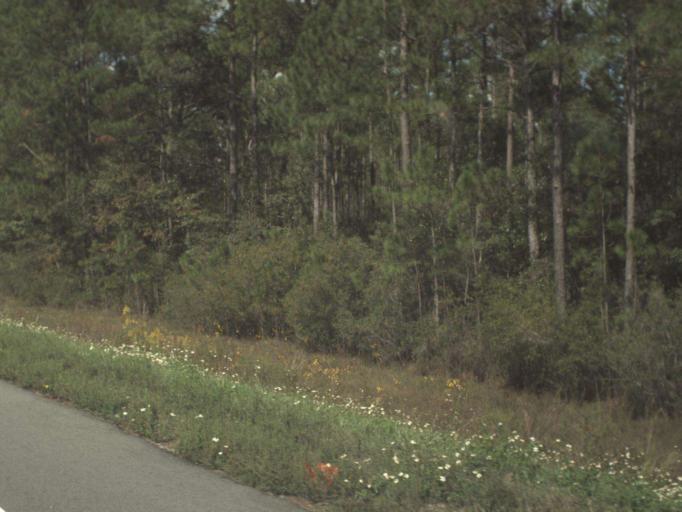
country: US
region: Florida
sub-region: Walton County
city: Freeport
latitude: 30.4589
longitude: -85.9218
